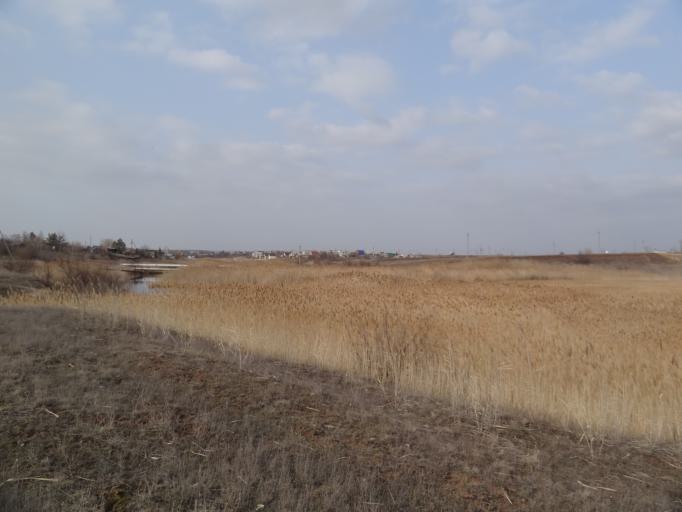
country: RU
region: Saratov
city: Shumeyka
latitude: 51.4885
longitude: 46.2770
